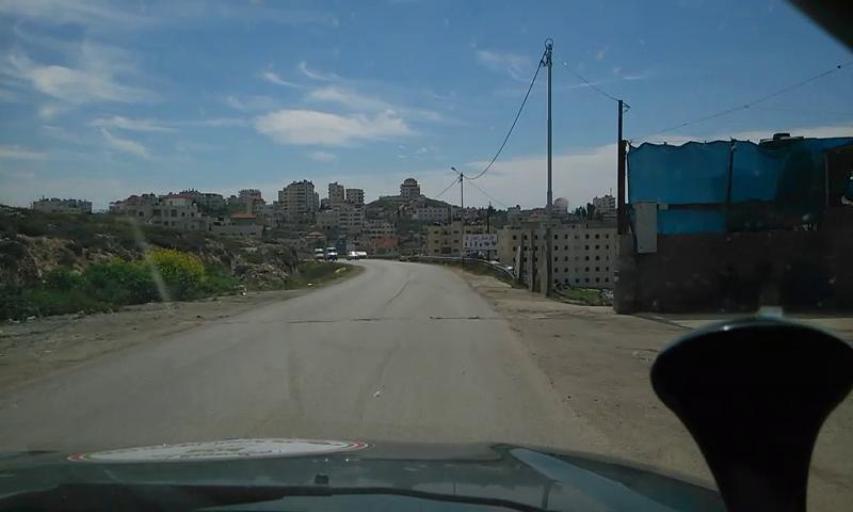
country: PS
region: West Bank
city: Al Judayrah
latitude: 31.8551
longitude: 35.2015
